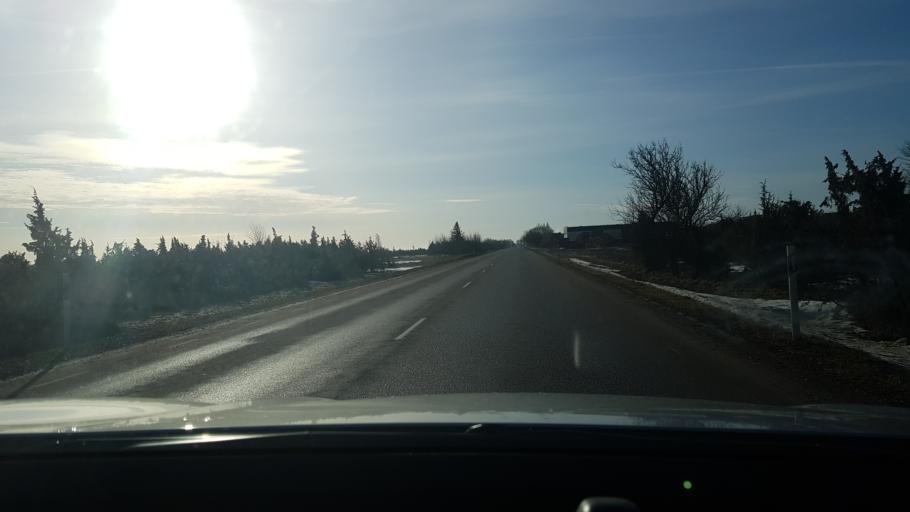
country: EE
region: Saare
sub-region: Kuressaare linn
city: Kuressaare
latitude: 58.2300
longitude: 22.5049
